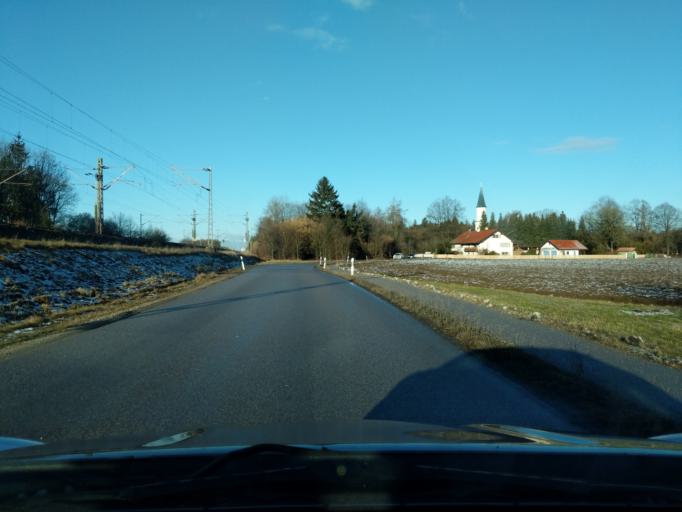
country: DE
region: Bavaria
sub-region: Upper Bavaria
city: Zorneding
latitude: 48.0852
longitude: 11.8562
